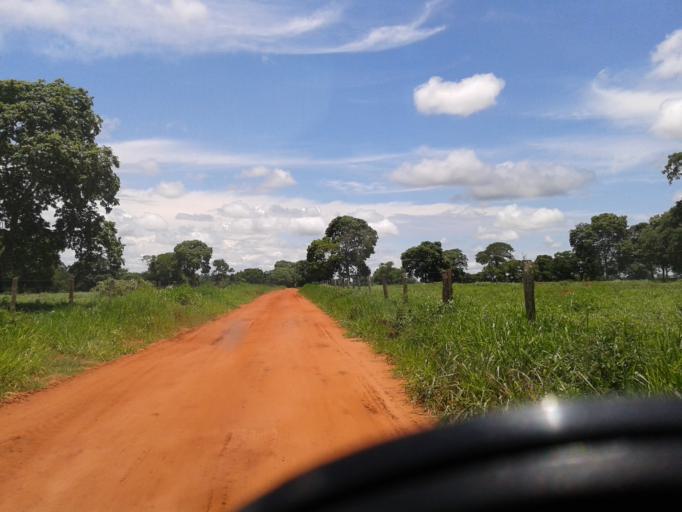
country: BR
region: Minas Gerais
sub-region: Santa Vitoria
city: Santa Vitoria
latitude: -18.9521
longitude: -49.8634
